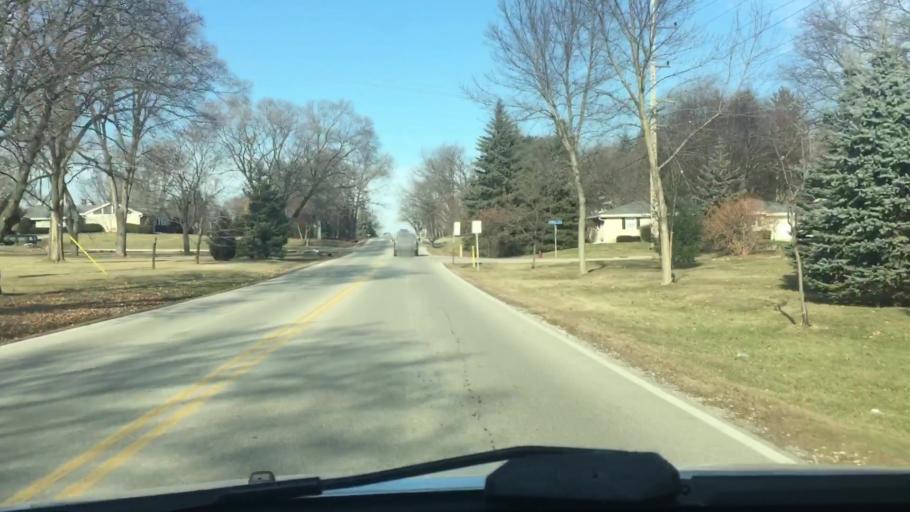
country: US
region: Wisconsin
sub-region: Waukesha County
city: Elm Grove
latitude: 43.0545
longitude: -88.0668
